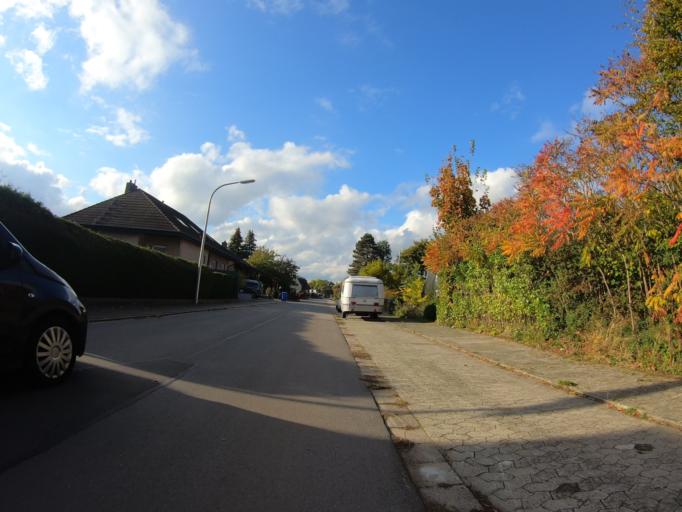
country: DE
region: Lower Saxony
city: Wagenhoff
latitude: 52.5166
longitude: 10.5451
